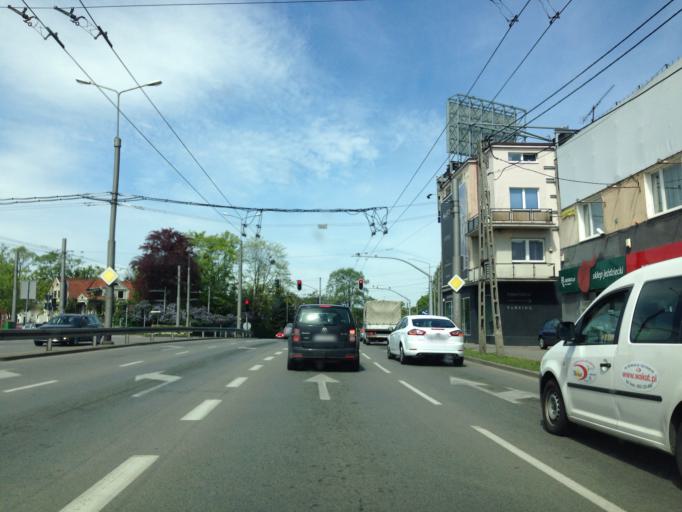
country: PL
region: Pomeranian Voivodeship
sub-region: Gdynia
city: Gdynia
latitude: 54.4845
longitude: 18.5466
